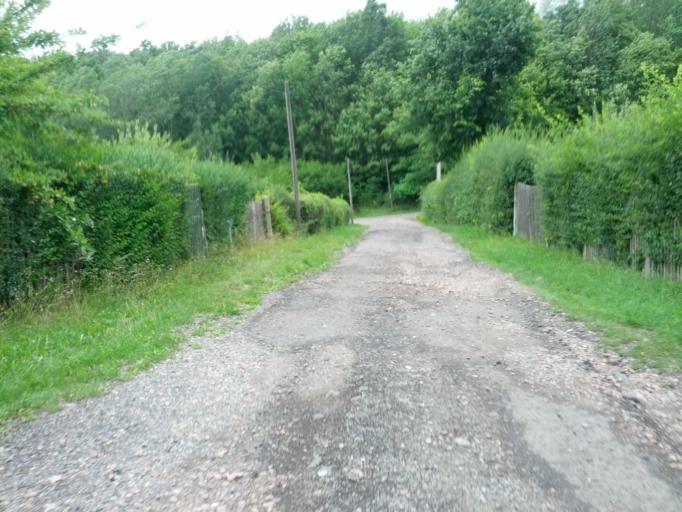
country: DE
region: Thuringia
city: Eisenach
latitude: 50.9865
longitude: 10.3432
